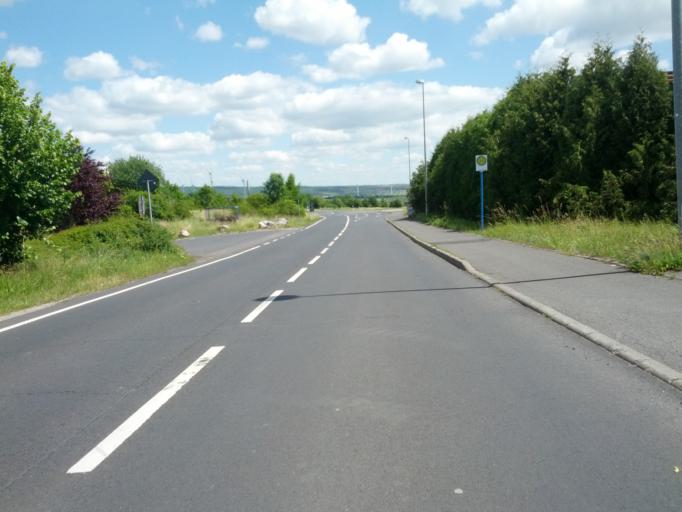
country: DE
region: Thuringia
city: Eisenach
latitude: 50.9940
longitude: 10.3527
